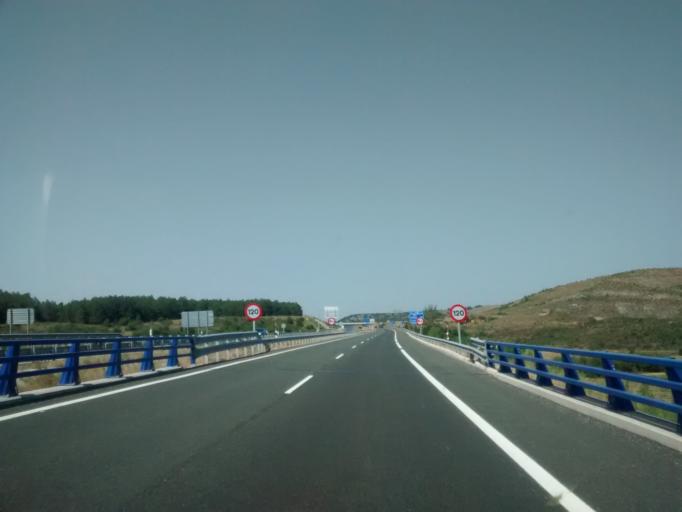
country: ES
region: Castille and Leon
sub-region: Provincia de Palencia
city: Aguilar de Campoo
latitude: 42.7721
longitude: -4.2560
